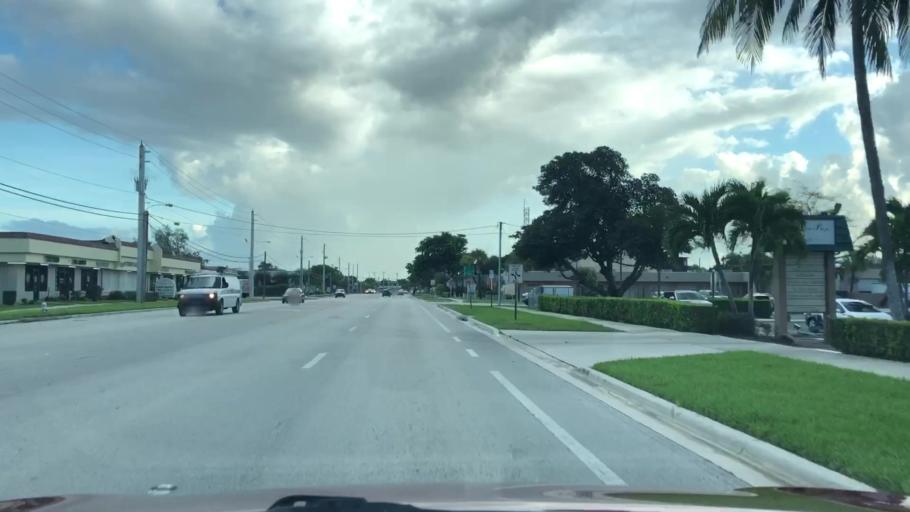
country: US
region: Florida
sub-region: Palm Beach County
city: Boca Raton
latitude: 26.3638
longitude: -80.0901
